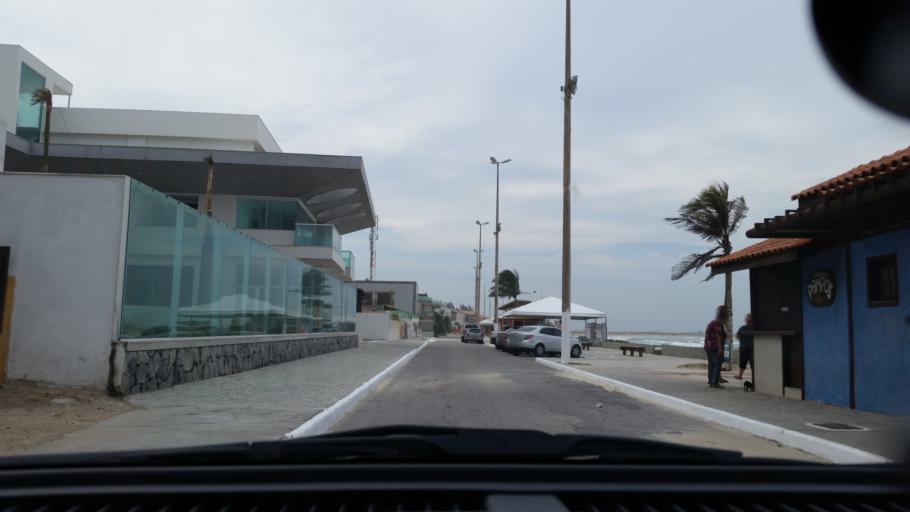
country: BR
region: Rio de Janeiro
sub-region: Cabo Frio
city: Cabo Frio
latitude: -22.8625
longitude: -41.9860
